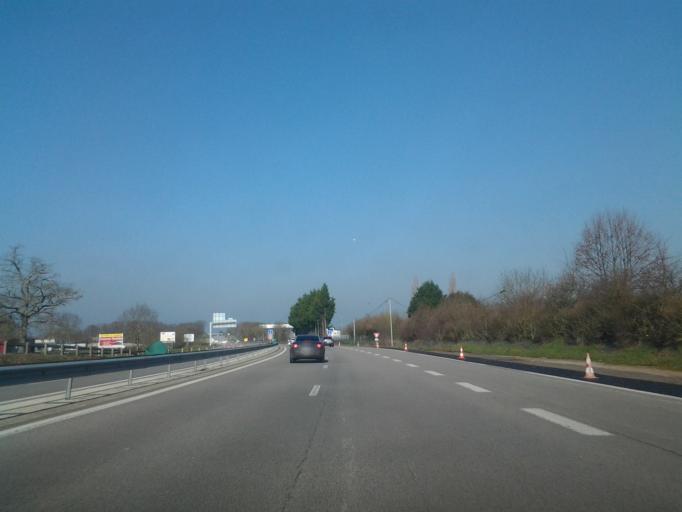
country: FR
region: Pays de la Loire
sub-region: Departement de la Vendee
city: Aizenay
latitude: 46.7481
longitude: -1.6242
